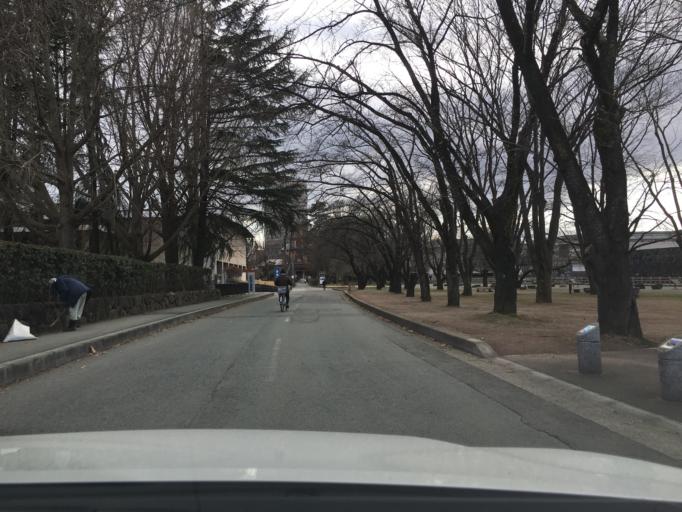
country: JP
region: Yamagata
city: Yamagata-shi
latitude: 38.2553
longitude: 140.3297
